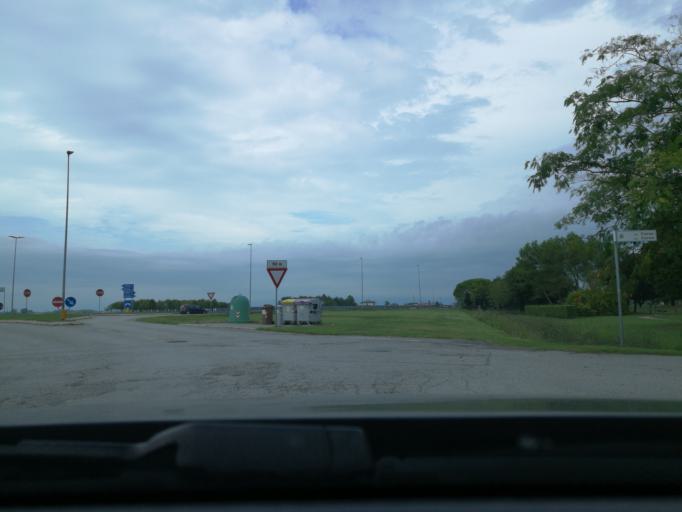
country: IT
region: Friuli Venezia Giulia
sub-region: Provincia di Udine
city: Pertegada
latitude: 45.7228
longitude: 13.0685
